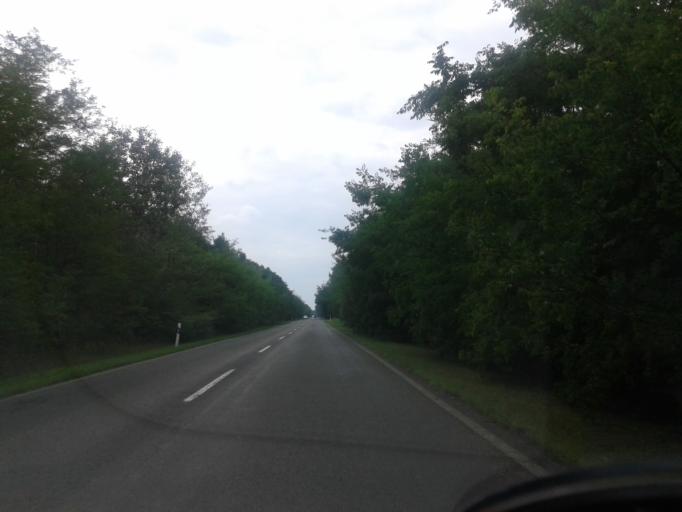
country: HU
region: Csongrad
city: Ruzsa
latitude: 46.2353
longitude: 19.7269
